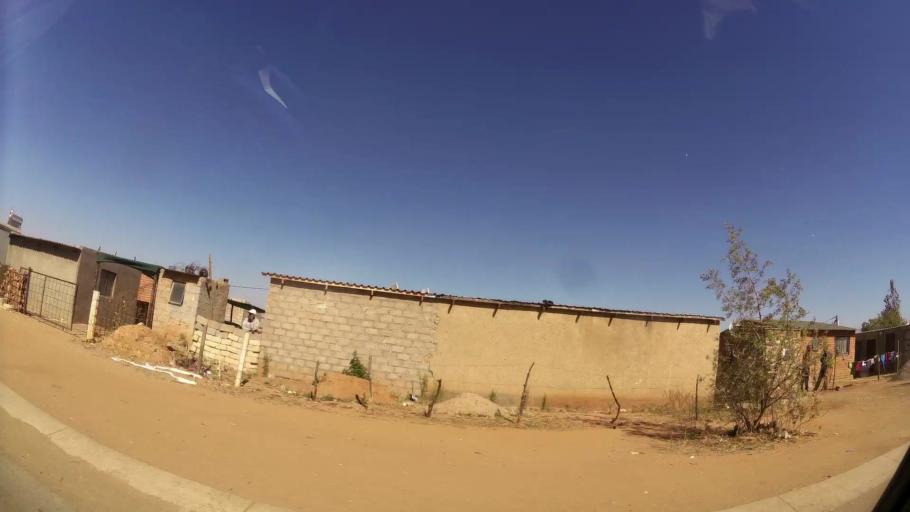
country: ZA
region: Gauteng
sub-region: City of Johannesburg Metropolitan Municipality
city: Diepsloot
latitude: -25.9048
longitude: 28.0914
